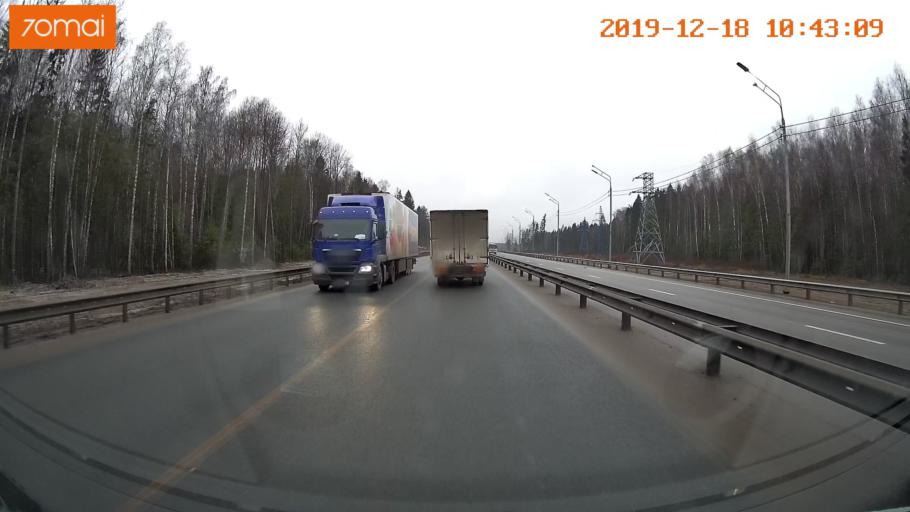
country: RU
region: Moskovskaya
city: Aprelevka
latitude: 55.4664
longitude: 37.0869
